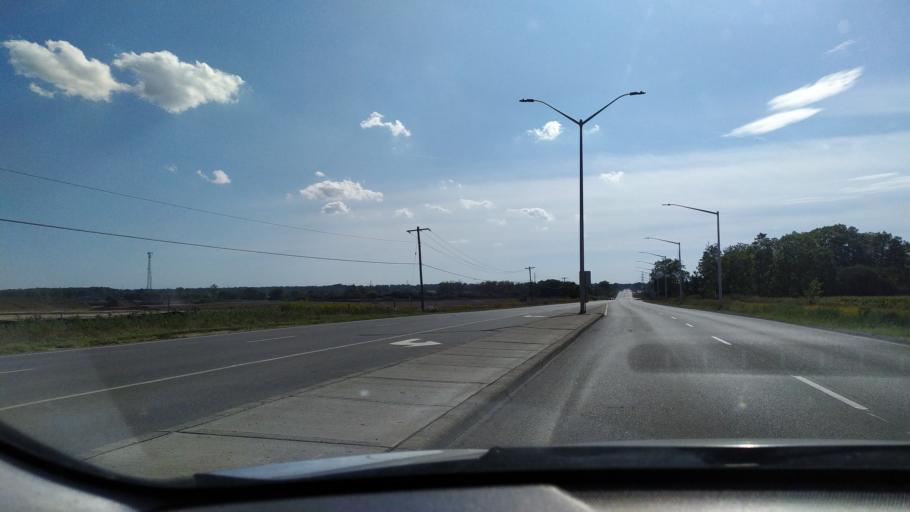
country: CA
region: Ontario
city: London
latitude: 42.9315
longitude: -81.2680
